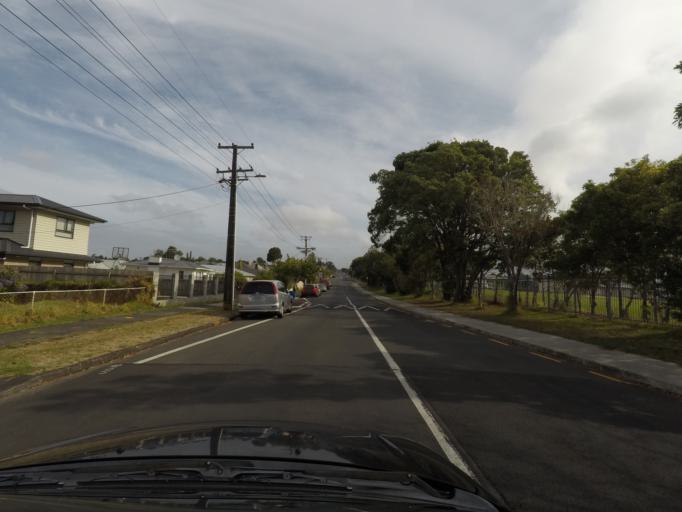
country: NZ
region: Auckland
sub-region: Auckland
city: Waitakere
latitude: -36.8985
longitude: 174.6675
